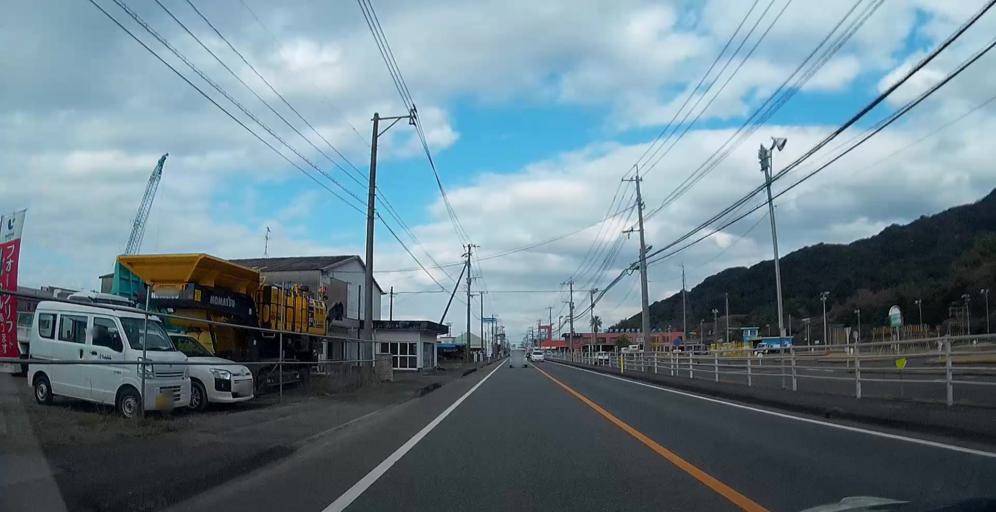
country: JP
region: Kumamoto
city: Yatsushiro
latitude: 32.4679
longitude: 130.6056
